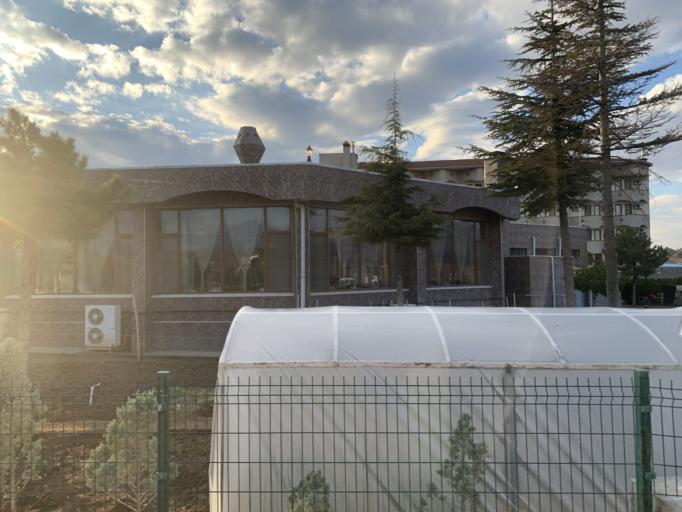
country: TR
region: Nevsehir
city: Avanos
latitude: 38.7028
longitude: 34.8387
